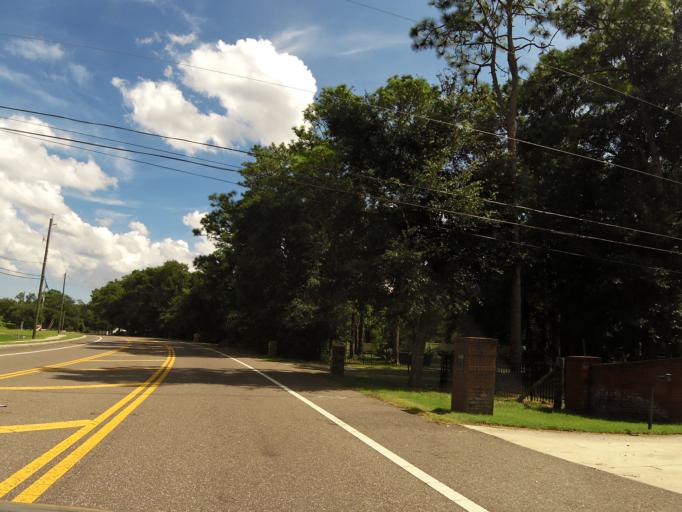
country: US
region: Florida
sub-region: Duval County
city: Jacksonville
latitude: 30.4264
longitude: -81.5801
